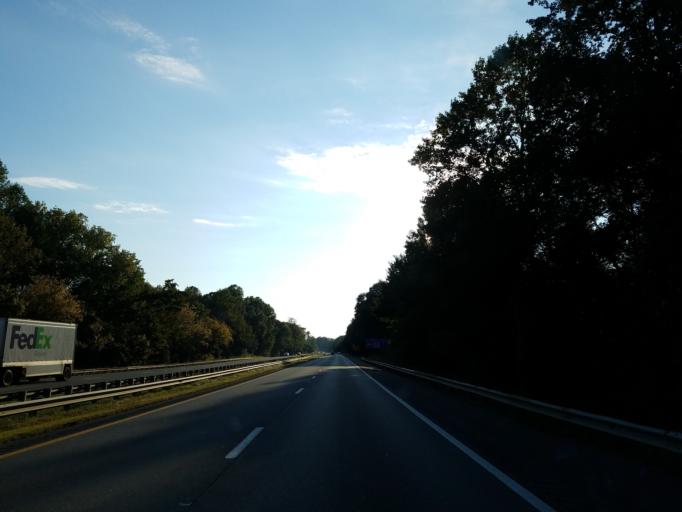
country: US
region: North Carolina
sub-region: Cleveland County
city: White Plains
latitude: 35.1695
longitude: -81.4368
